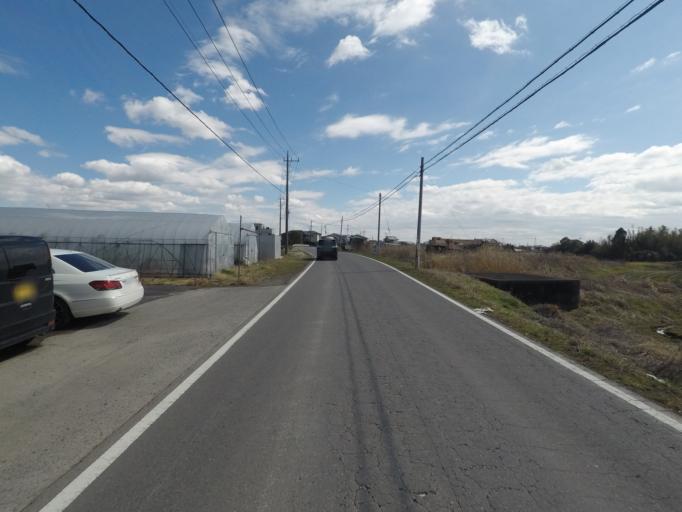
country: JP
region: Ibaraki
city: Fujishiro
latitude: 35.9455
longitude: 140.0863
